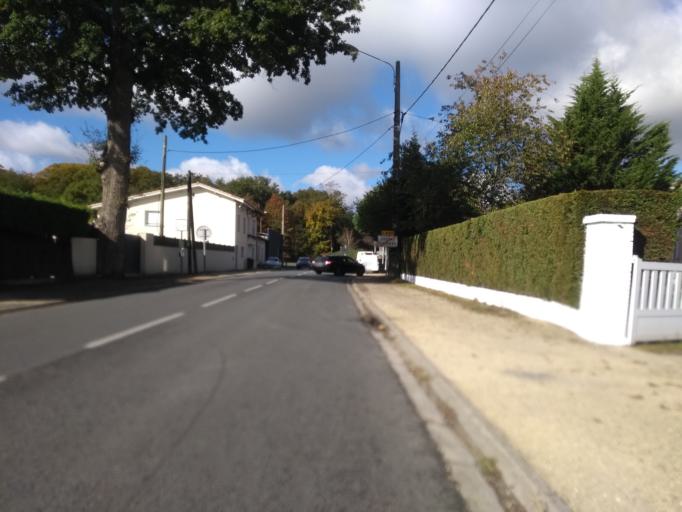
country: FR
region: Aquitaine
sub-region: Departement de la Gironde
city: Saint-Aubin-de-Medoc
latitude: 44.7746
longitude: -0.7048
